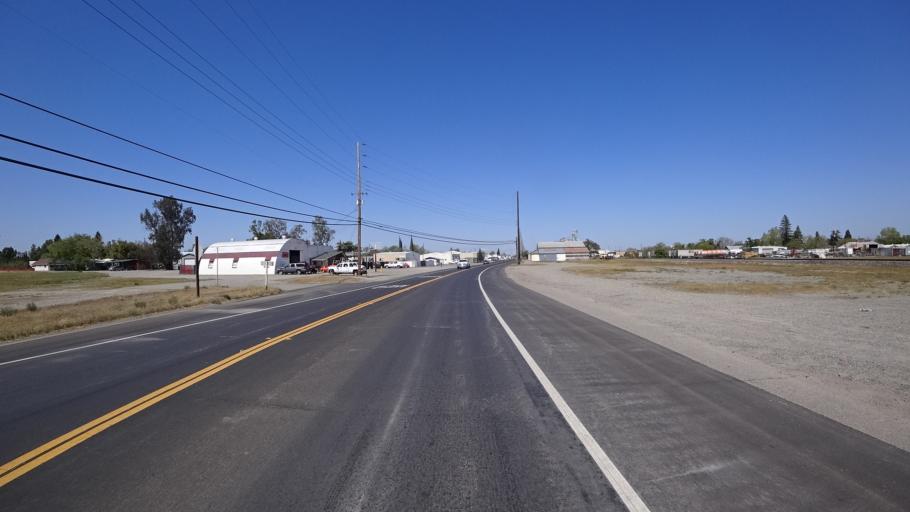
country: US
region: California
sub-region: Glenn County
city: Orland
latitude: 39.7411
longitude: -122.1975
